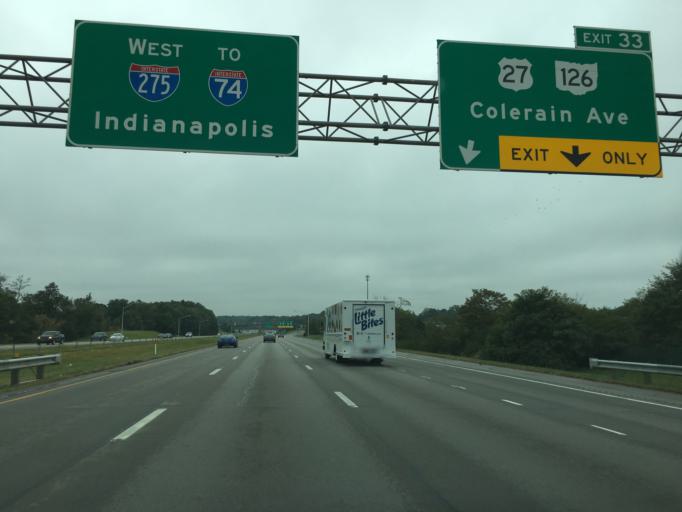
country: US
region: Ohio
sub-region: Hamilton County
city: Northgate
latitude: 39.2613
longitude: -84.5936
